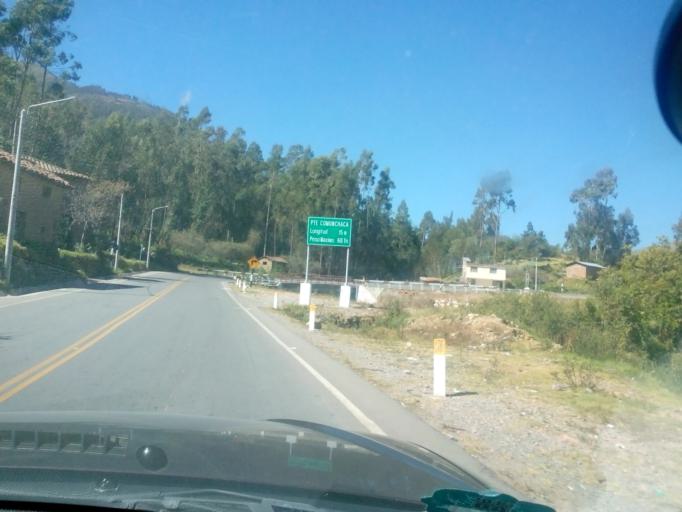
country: PE
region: Apurimac
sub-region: Chincheros
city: Chincheros
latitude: -13.5193
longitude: -73.7007
